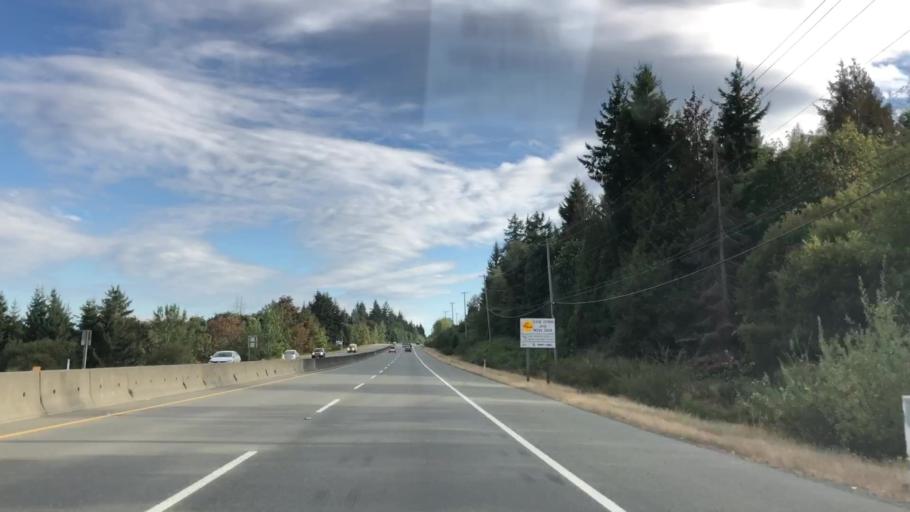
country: CA
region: British Columbia
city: North Saanich
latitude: 48.6364
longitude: -123.5505
